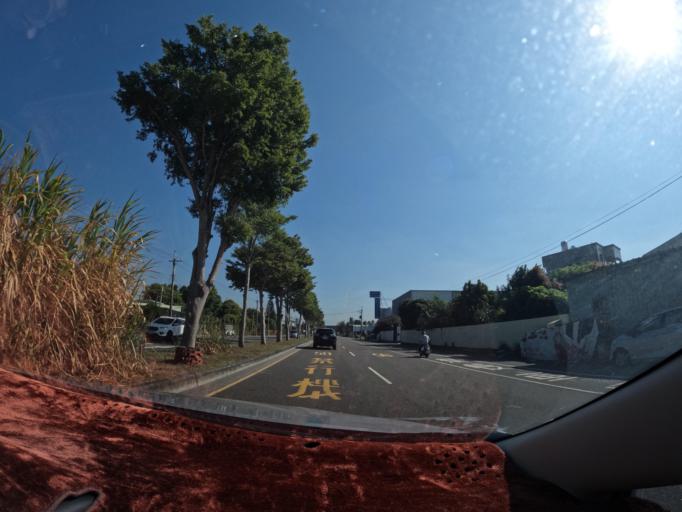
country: TW
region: Taiwan
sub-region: Tainan
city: Tainan
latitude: 23.0062
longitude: 120.2810
